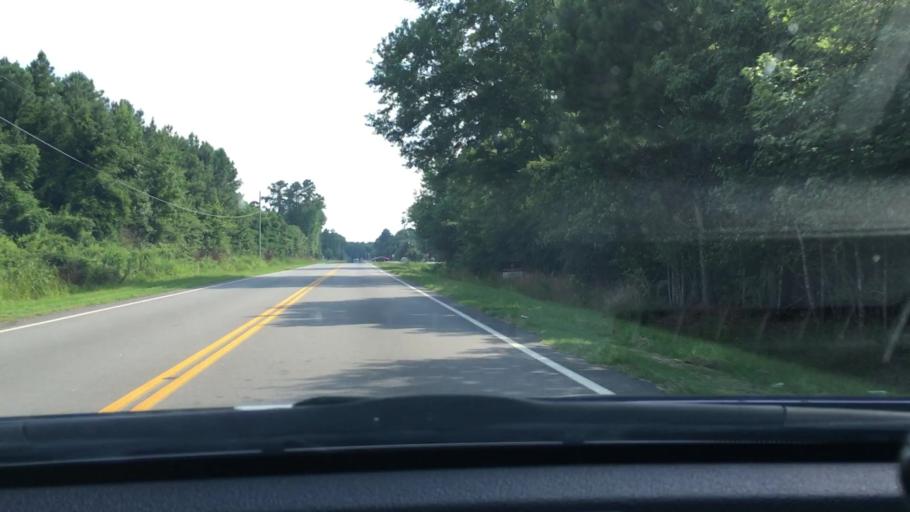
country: US
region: South Carolina
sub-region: Sumter County
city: Sumter
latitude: 33.9344
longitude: -80.3215
